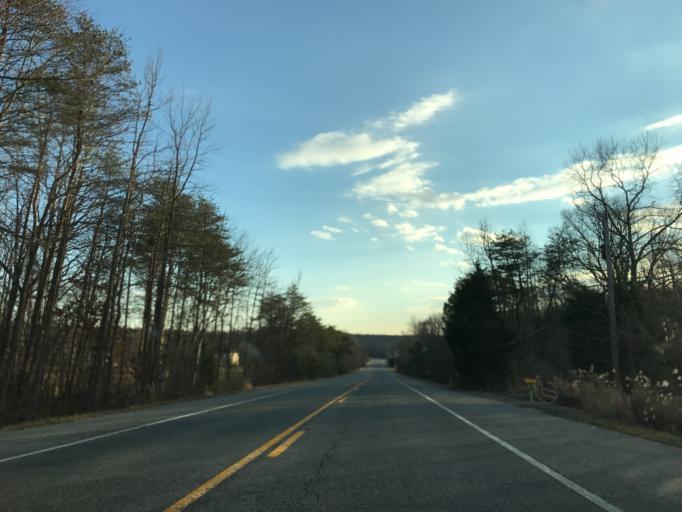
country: US
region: Maryland
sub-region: Cecil County
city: Charlestown
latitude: 39.5661
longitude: -75.9475
